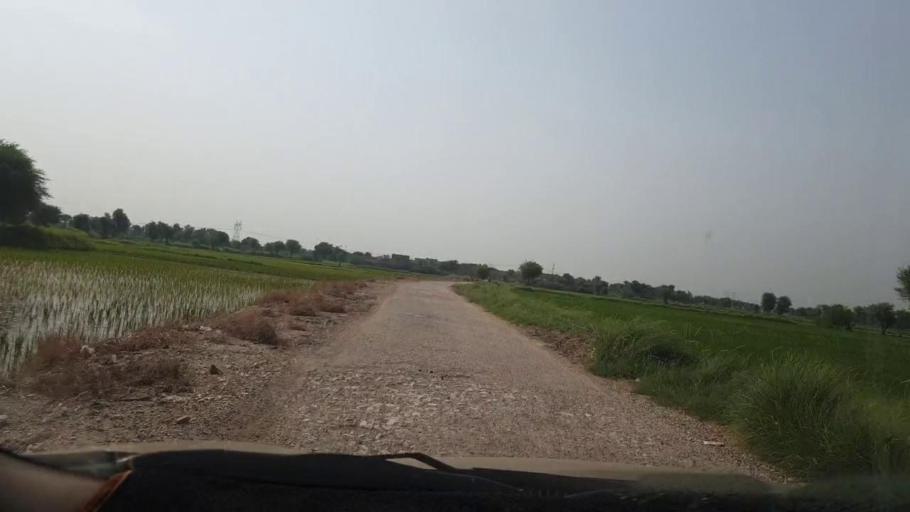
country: PK
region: Sindh
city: Goth Garelo
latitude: 27.4370
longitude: 68.0423
